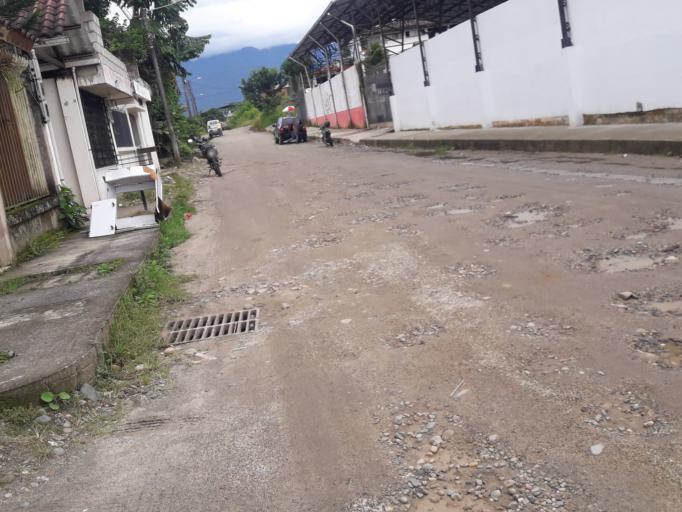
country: EC
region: Napo
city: Tena
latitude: -0.9842
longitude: -77.8200
